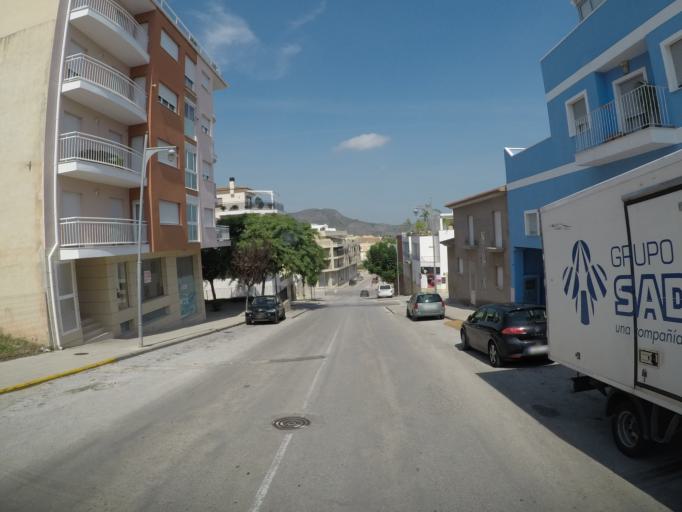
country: ES
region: Valencia
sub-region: Provincia de Alicante
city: Pego
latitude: 38.8422
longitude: -0.1130
